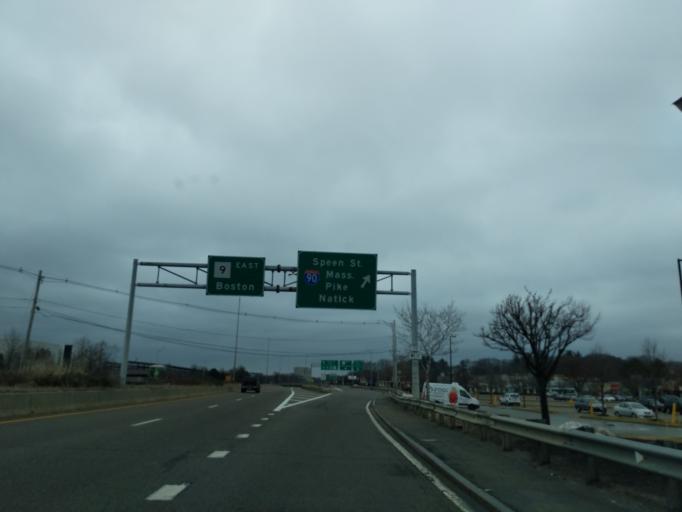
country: US
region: Massachusetts
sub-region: Middlesex County
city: Cochituate
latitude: 42.2990
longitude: -71.3858
